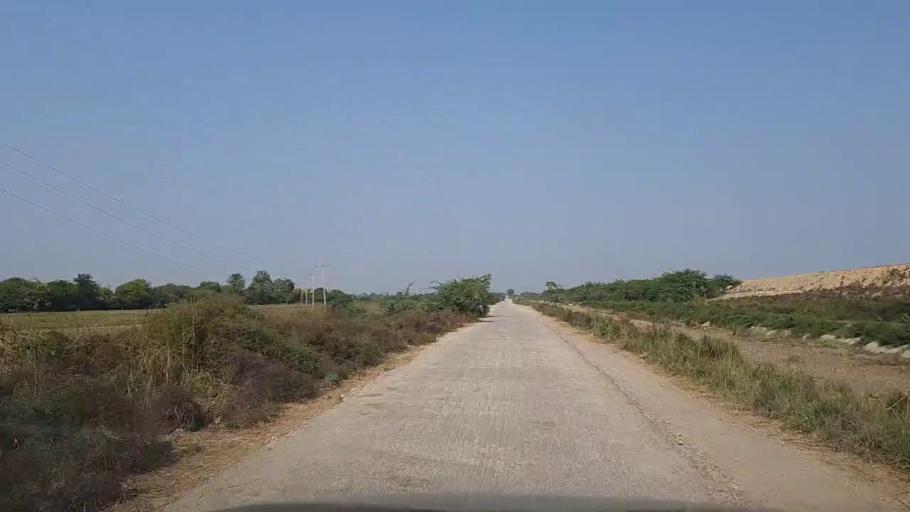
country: PK
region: Sindh
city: Chuhar Jamali
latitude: 24.5198
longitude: 67.9258
